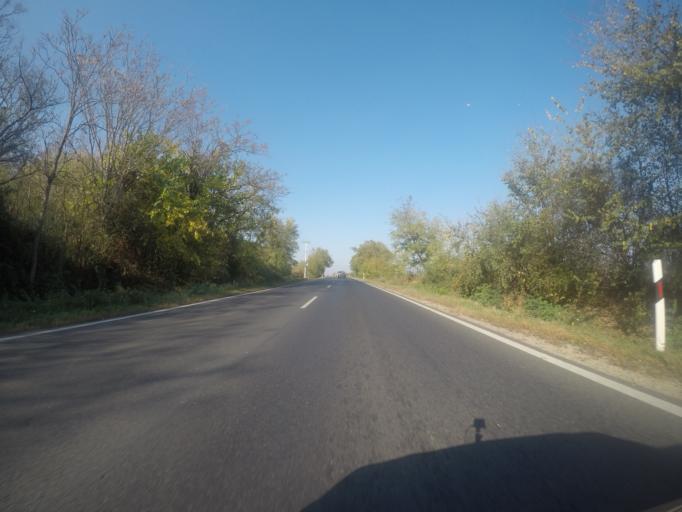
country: HU
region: Tolna
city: Dunafoldvar
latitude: 46.8376
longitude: 18.9099
